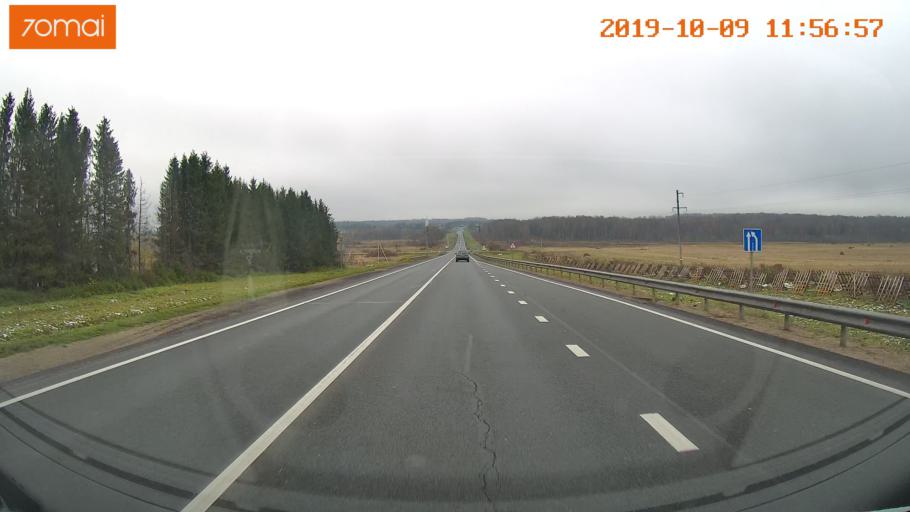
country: RU
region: Vologda
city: Gryazovets
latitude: 58.7383
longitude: 40.2901
